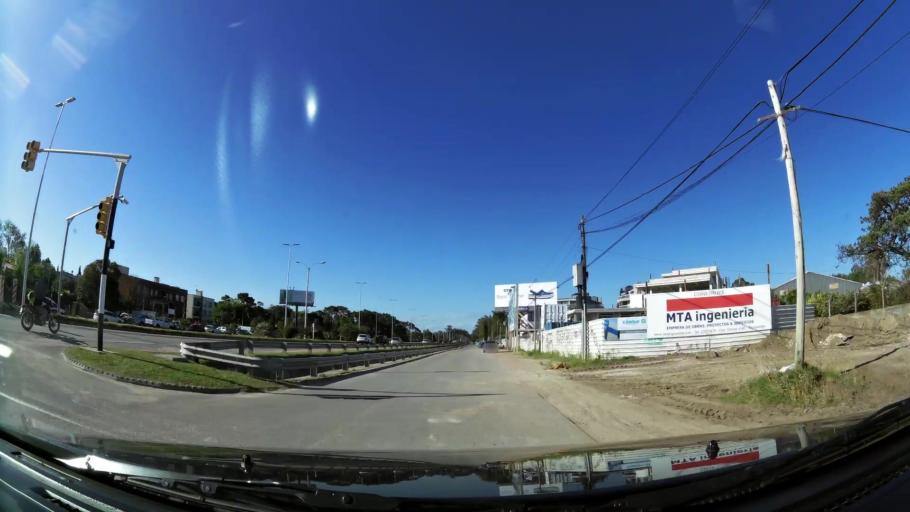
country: UY
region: Canelones
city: Barra de Carrasco
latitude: -34.8706
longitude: -56.0316
